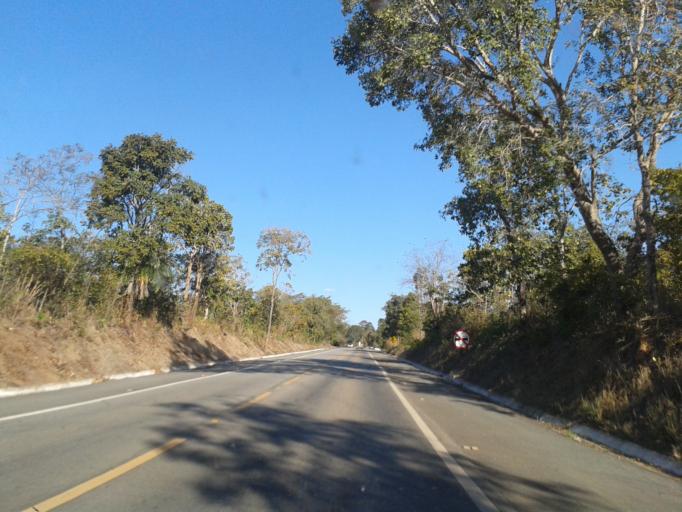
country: BR
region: Goias
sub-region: Itapuranga
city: Itapuranga
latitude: -15.3511
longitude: -50.4058
